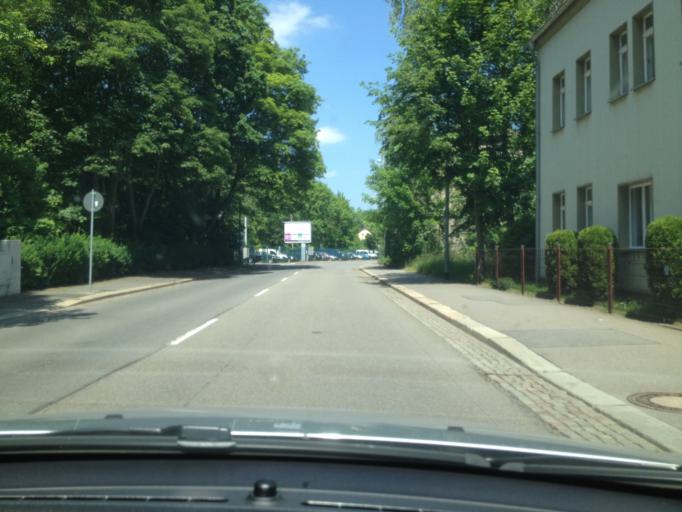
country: DE
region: Saxony
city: Burkhardtsdorf
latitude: 50.7825
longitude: 12.9251
